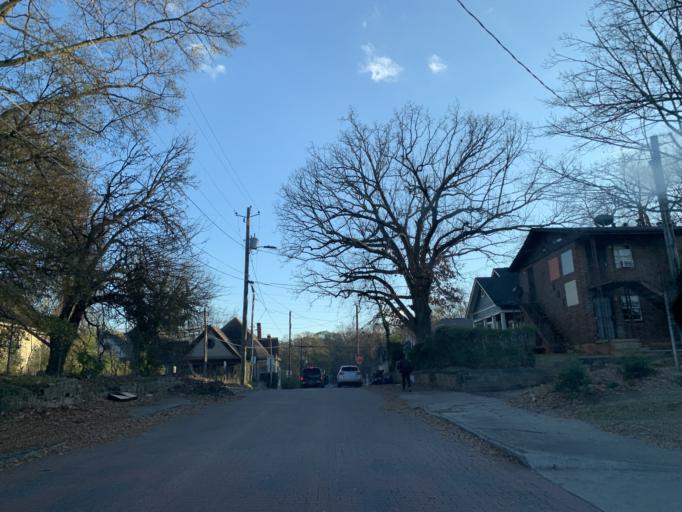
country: US
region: Georgia
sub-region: Fulton County
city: Atlanta
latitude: 33.7362
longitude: -84.3959
